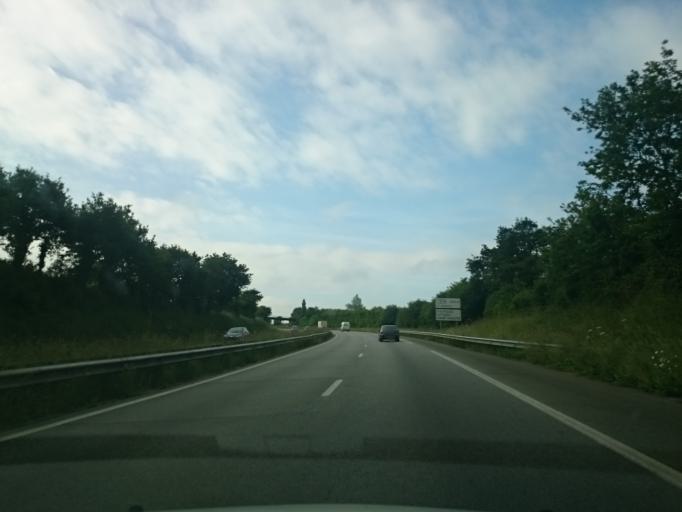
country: FR
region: Brittany
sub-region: Departement du Finistere
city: Chateaulin
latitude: 48.1675
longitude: -4.0478
